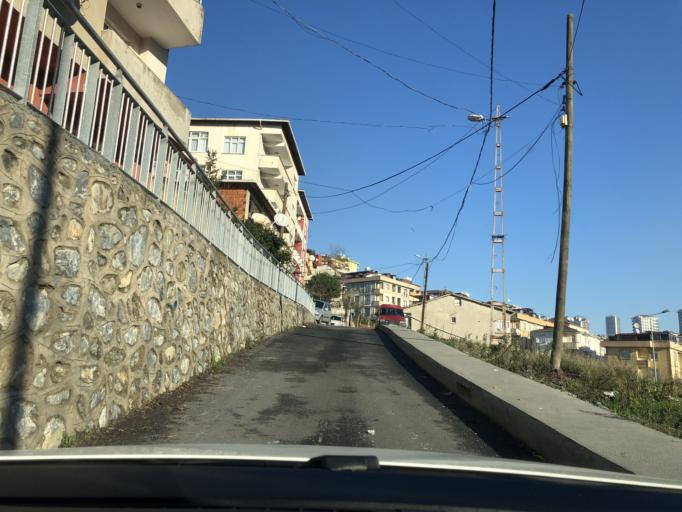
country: TR
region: Istanbul
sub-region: Atasehir
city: Atasehir
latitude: 40.9704
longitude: 29.1228
